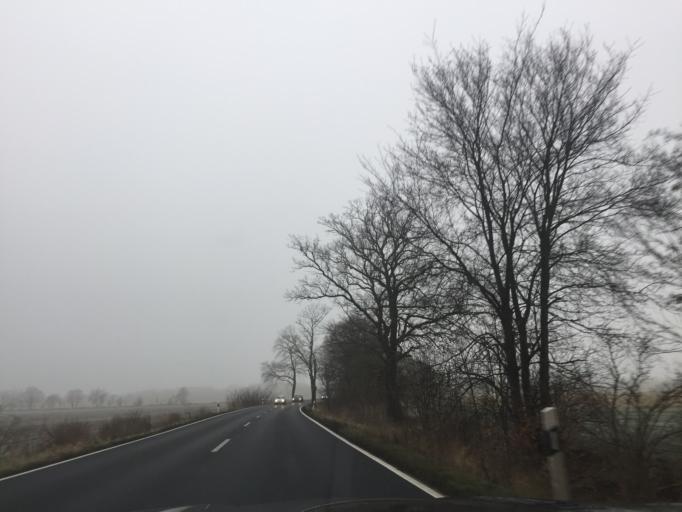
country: DE
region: Brandenburg
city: Velten
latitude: 52.6611
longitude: 13.1726
